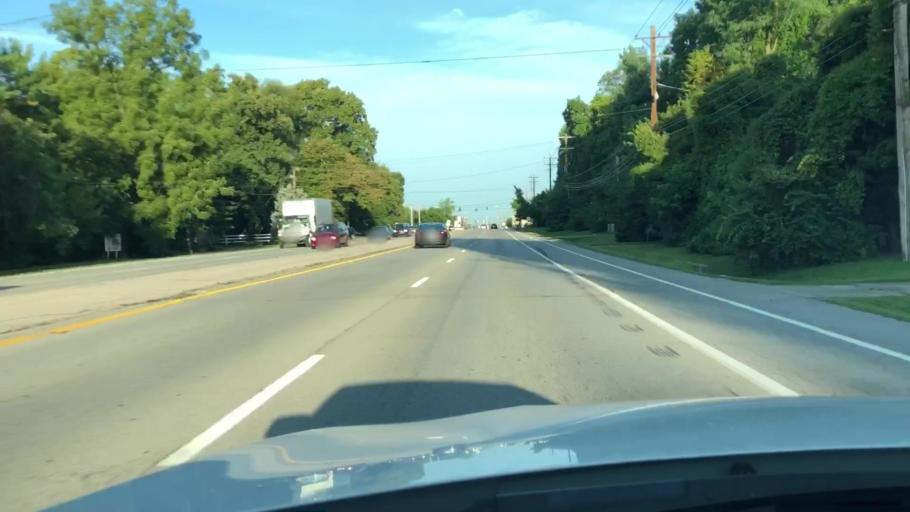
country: US
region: Kentucky
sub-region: Jefferson County
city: Saint Regis Park
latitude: 38.2195
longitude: -85.6168
